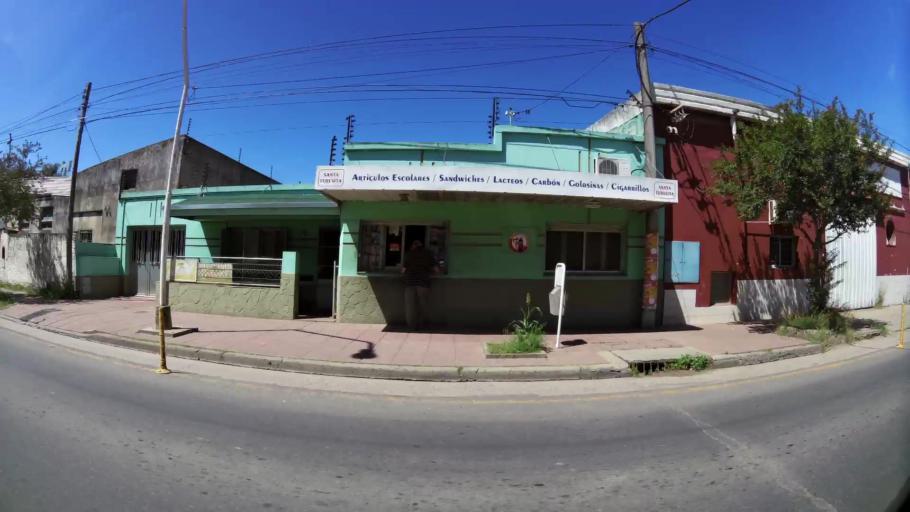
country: AR
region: Santa Fe
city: Esperanza
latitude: -31.4447
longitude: -60.9208
